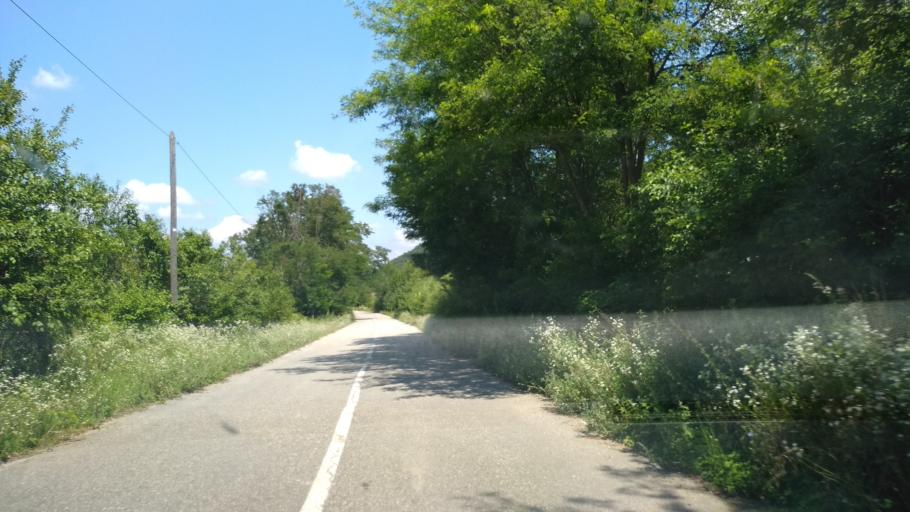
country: RO
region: Hunedoara
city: Berca
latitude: 45.6077
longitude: 23.0222
